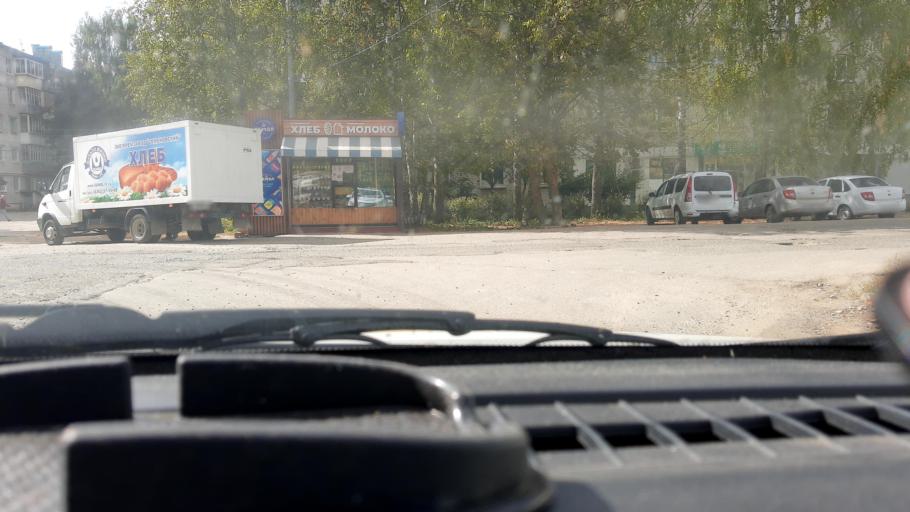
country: RU
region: Mariy-El
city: Medvedevo
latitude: 56.6361
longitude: 47.7982
